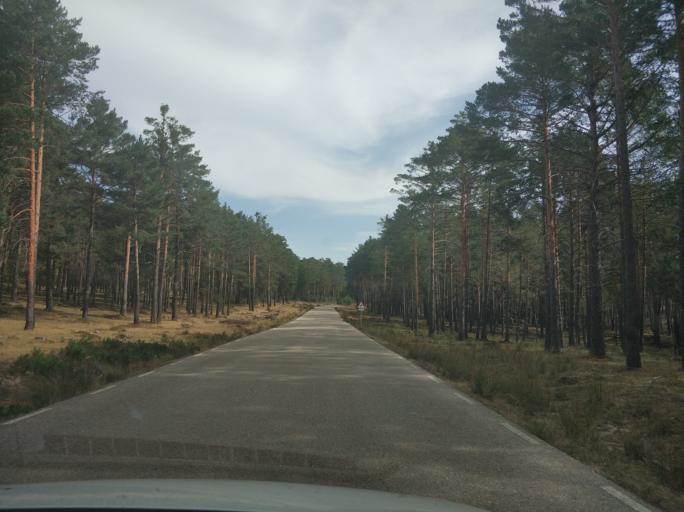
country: ES
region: Castille and Leon
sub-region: Provincia de Soria
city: Navaleno
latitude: 41.8693
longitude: -2.9439
